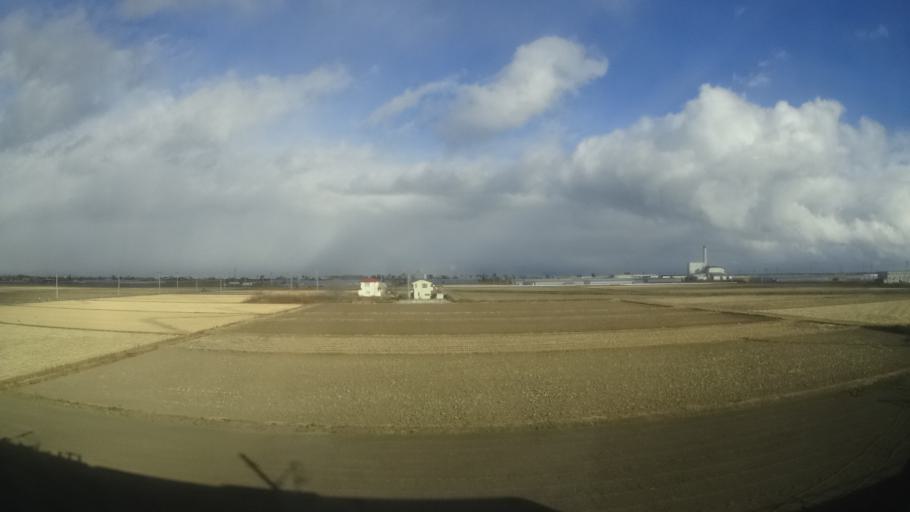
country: JP
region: Miyagi
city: Watari
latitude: 37.9566
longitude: 140.8922
